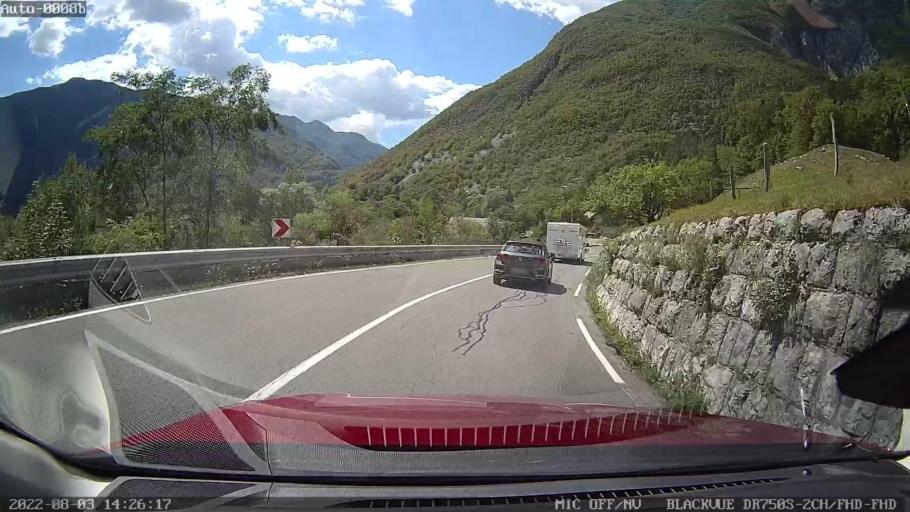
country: SI
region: Bovec
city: Bovec
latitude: 46.3151
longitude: 13.4988
